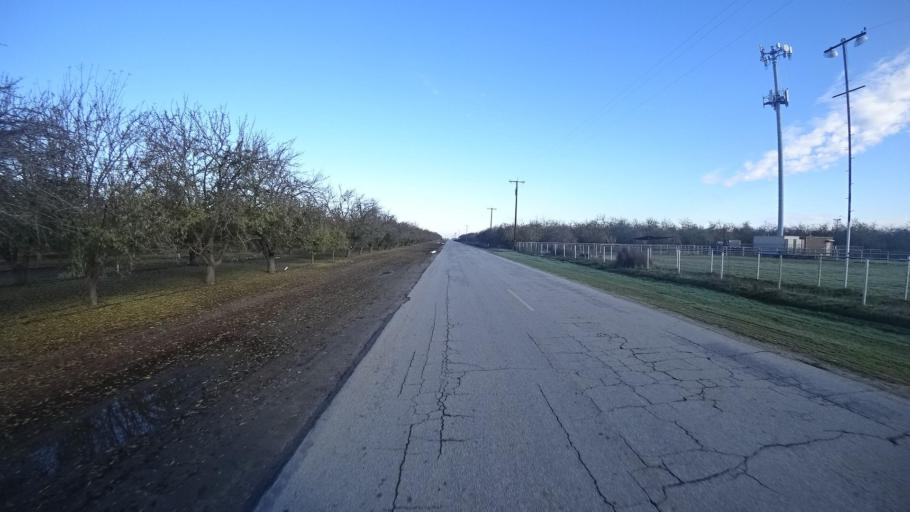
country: US
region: California
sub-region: Kern County
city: Delano
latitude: 35.7281
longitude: -119.3302
